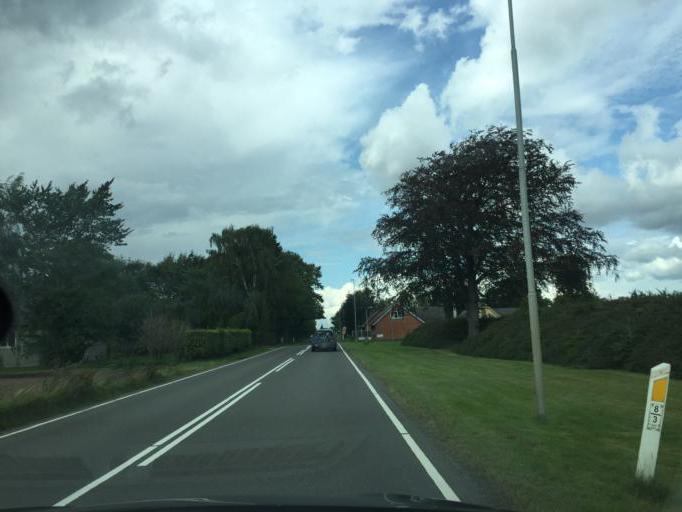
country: DK
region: South Denmark
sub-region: Odense Kommune
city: Stige
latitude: 55.4593
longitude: 10.3600
